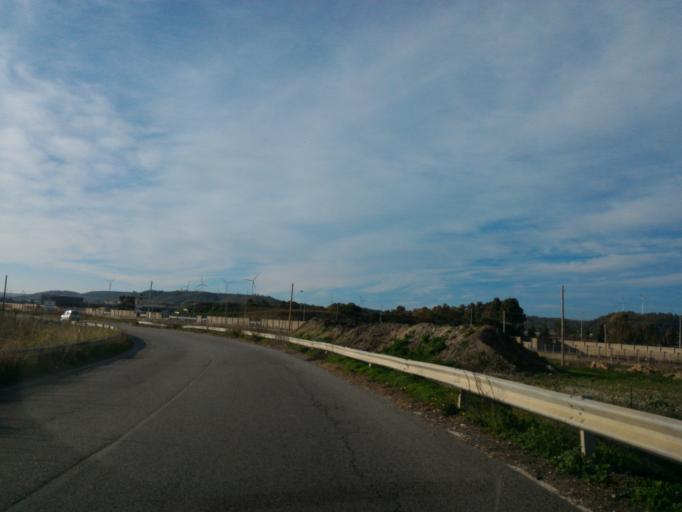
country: IT
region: Calabria
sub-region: Provincia di Crotone
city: Crotone
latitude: 39.1040
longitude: 17.1080
